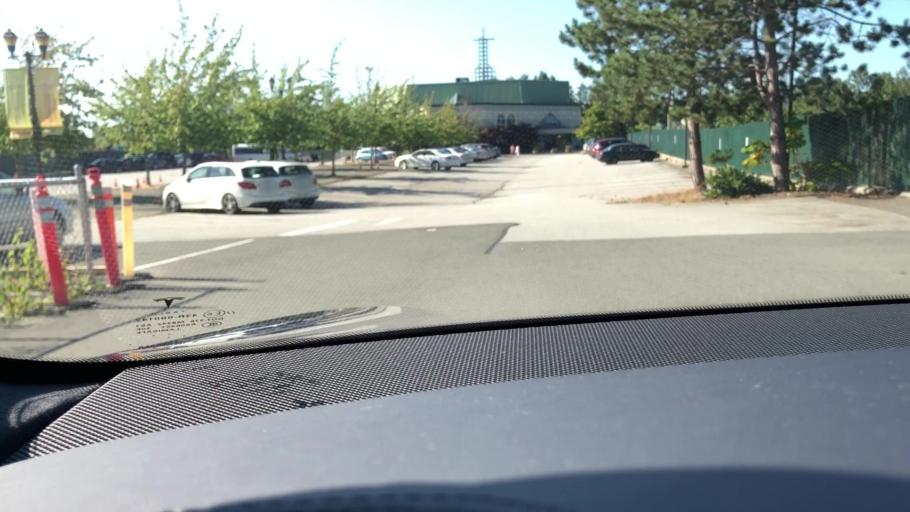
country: CA
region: British Columbia
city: Burnaby
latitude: 49.2063
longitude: -122.9905
